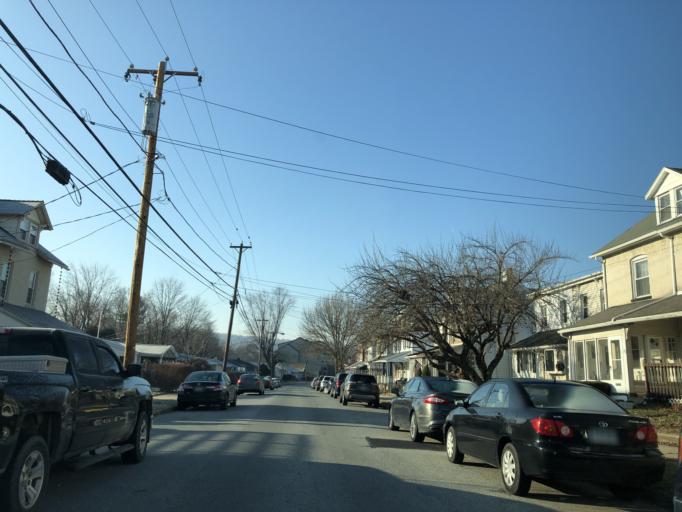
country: US
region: Pennsylvania
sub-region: Chester County
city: Downingtown
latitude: 40.0080
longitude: -75.6958
